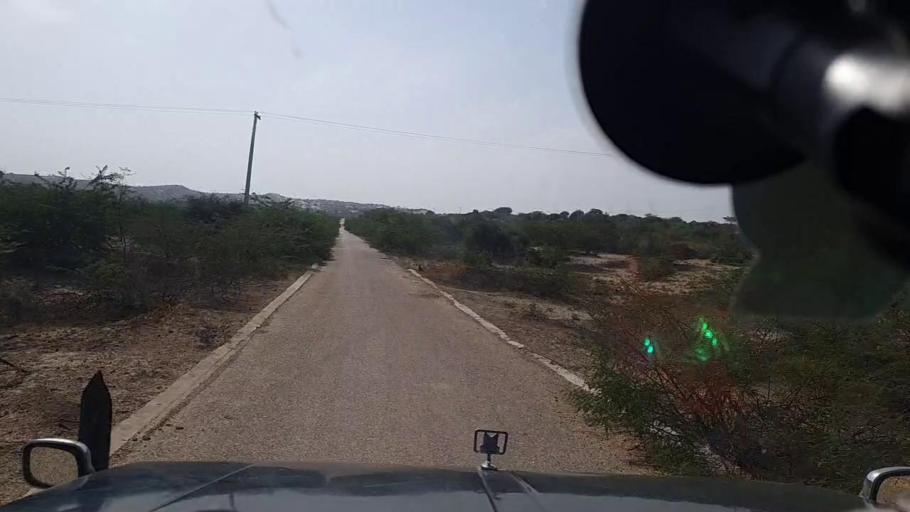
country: PK
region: Sindh
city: Diplo
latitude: 24.4201
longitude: 69.4724
